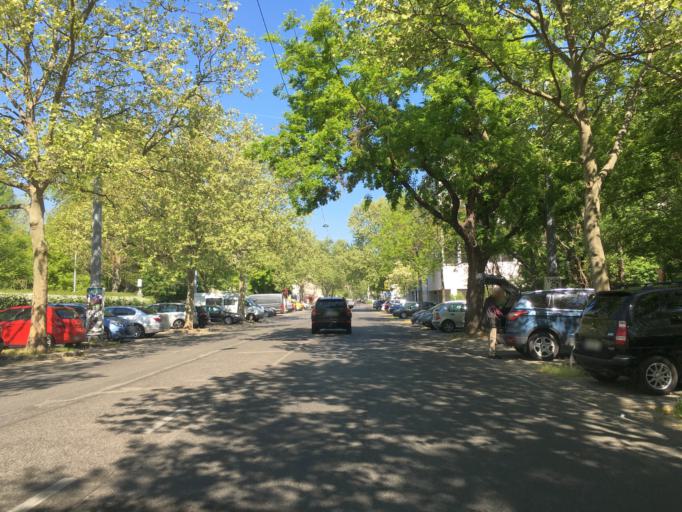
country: AT
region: Vienna
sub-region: Wien Stadt
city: Vienna
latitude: 48.2324
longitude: 16.3939
